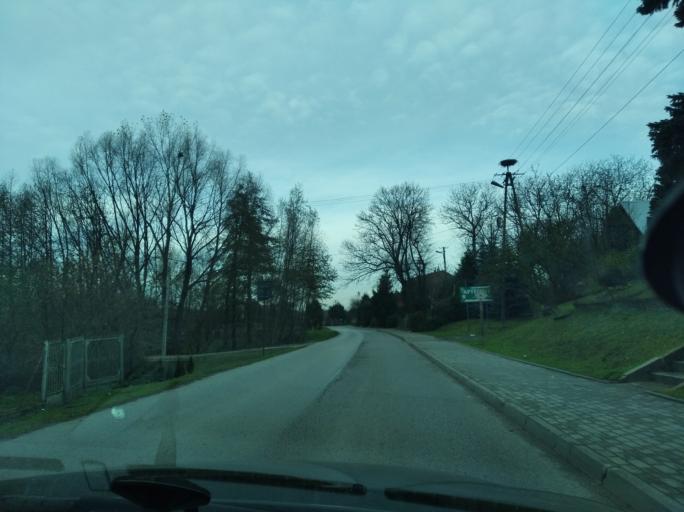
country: PL
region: Subcarpathian Voivodeship
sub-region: Powiat przeworski
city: Grzeska
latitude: 50.0772
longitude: 22.4540
